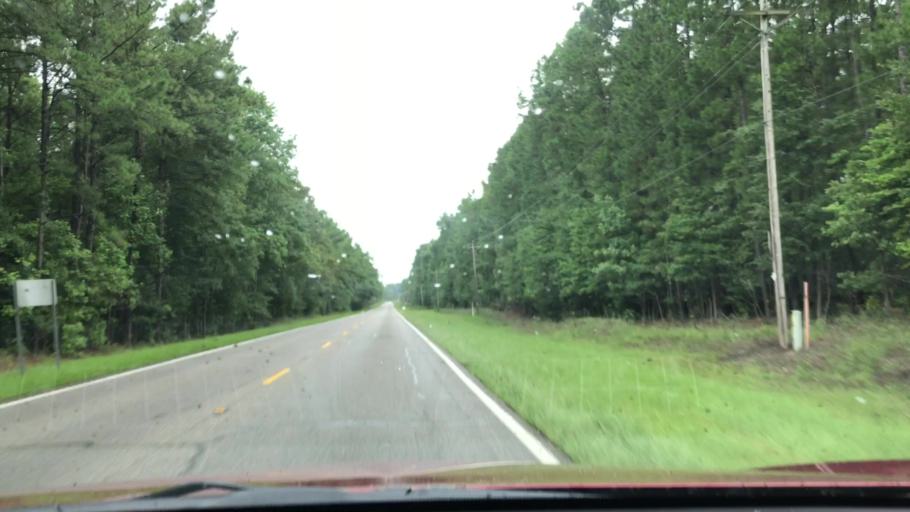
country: US
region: South Carolina
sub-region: Georgetown County
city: Georgetown
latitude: 33.4938
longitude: -79.2630
